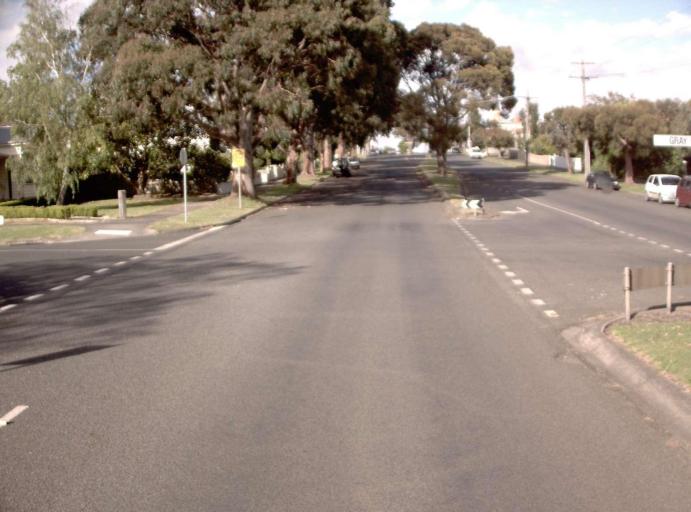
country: AU
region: Victoria
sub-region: Baw Baw
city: Warragul
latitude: -38.4793
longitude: 145.9417
